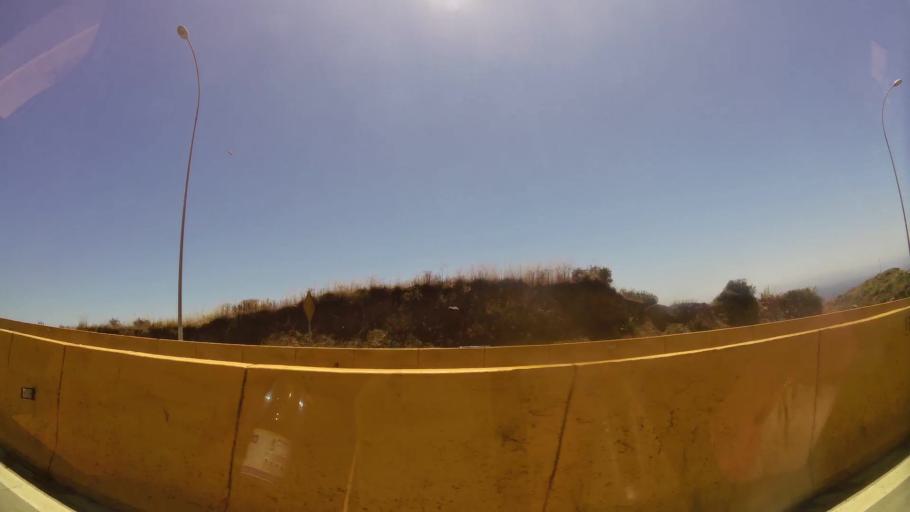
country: CL
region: Valparaiso
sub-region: Provincia de Valparaiso
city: Valparaiso
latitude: -33.0352
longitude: -71.6551
